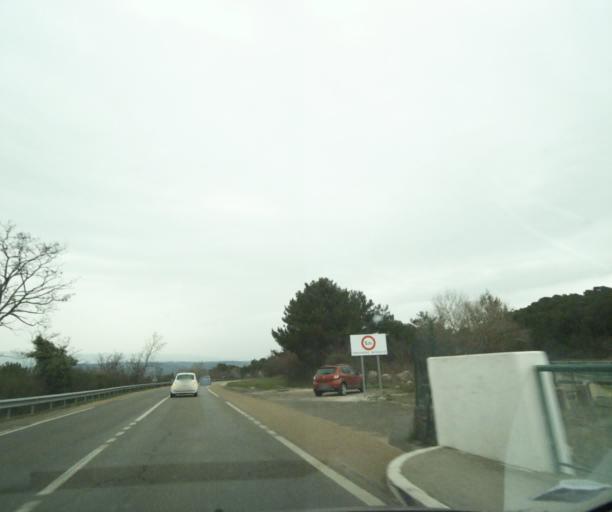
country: FR
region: Provence-Alpes-Cote d'Azur
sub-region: Departement des Bouches-du-Rhone
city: Le Puy-Sainte-Reparade
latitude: 43.6585
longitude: 5.4248
